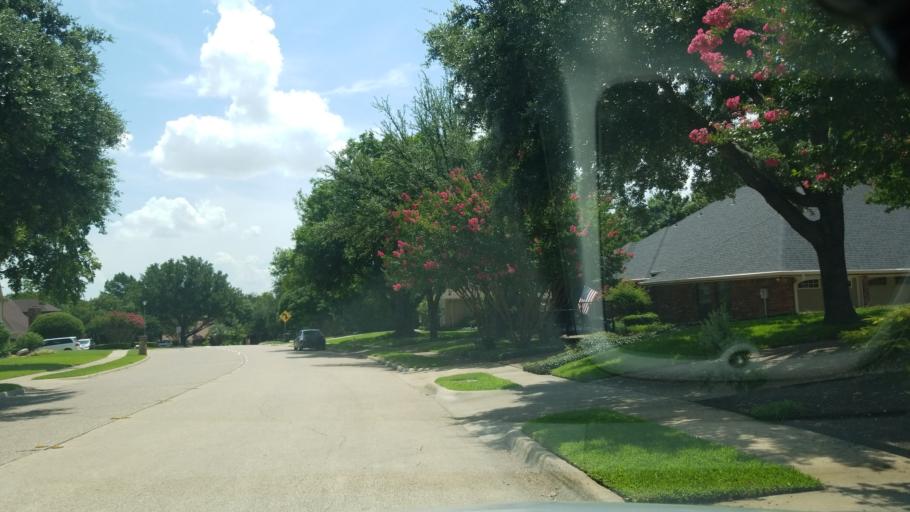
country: US
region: Texas
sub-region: Dallas County
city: Coppell
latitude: 32.9595
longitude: -96.9758
